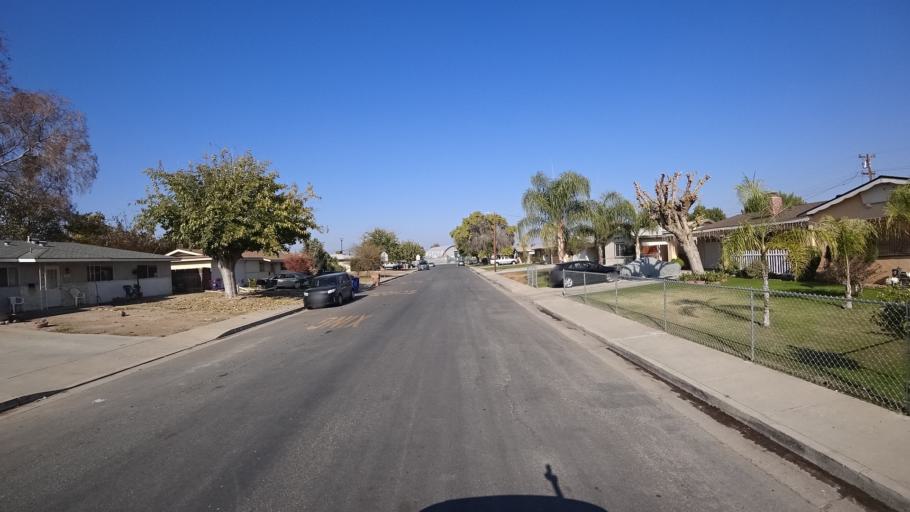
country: US
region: California
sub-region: Kern County
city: Greenfield
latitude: 35.3200
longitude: -119.0137
